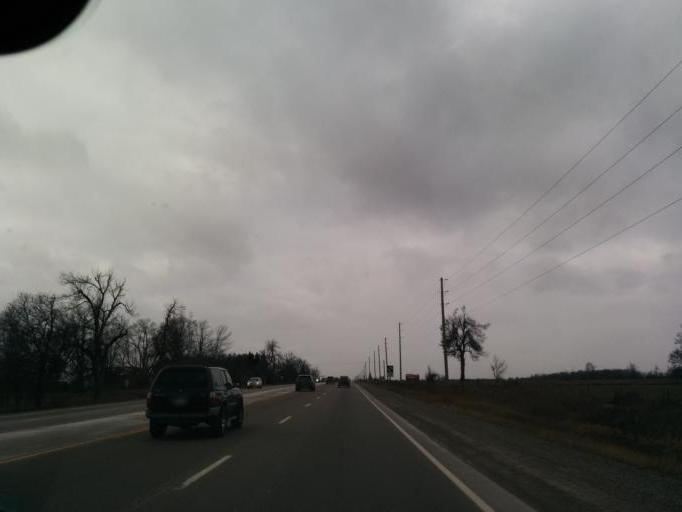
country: CA
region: Ontario
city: Brampton
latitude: 43.7554
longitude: -79.8539
